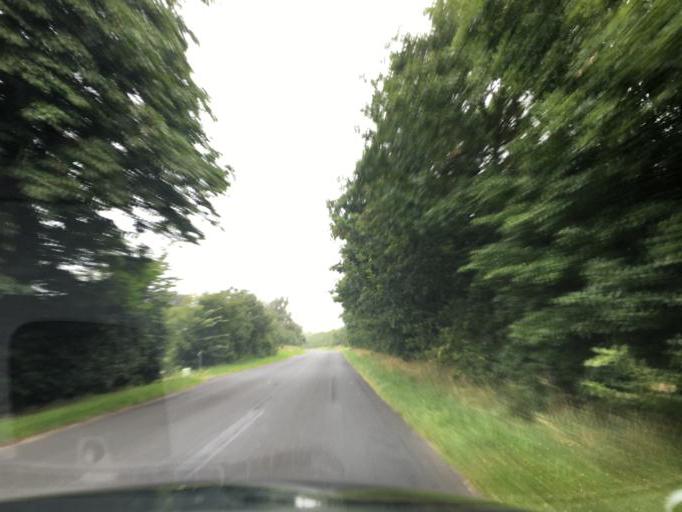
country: DK
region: South Denmark
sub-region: Kolding Kommune
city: Kolding
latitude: 55.5612
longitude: 9.4417
